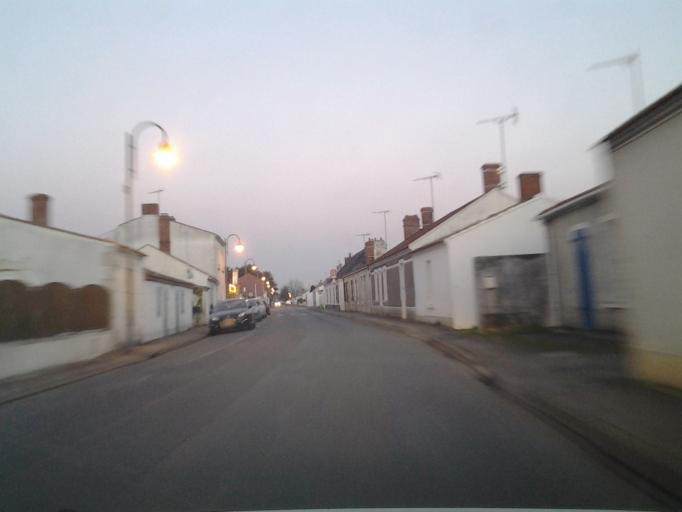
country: FR
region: Pays de la Loire
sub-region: Departement de la Vendee
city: Saint-Gervais
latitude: 46.9016
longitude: -1.9966
